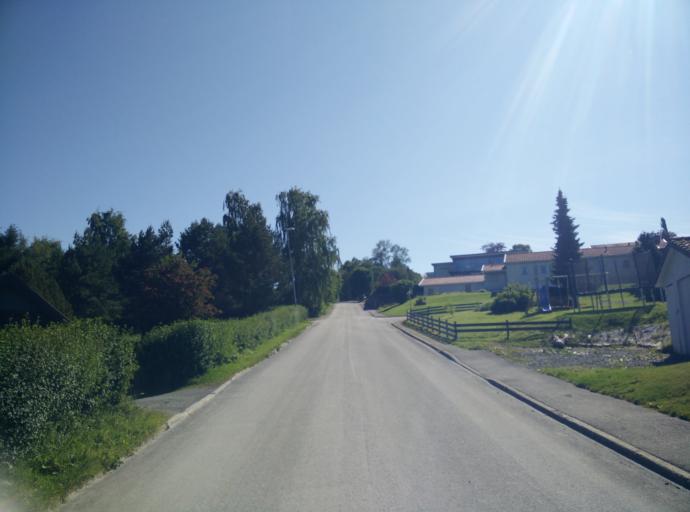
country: NO
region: Sor-Trondelag
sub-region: Trondheim
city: Trondheim
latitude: 63.4103
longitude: 10.3736
